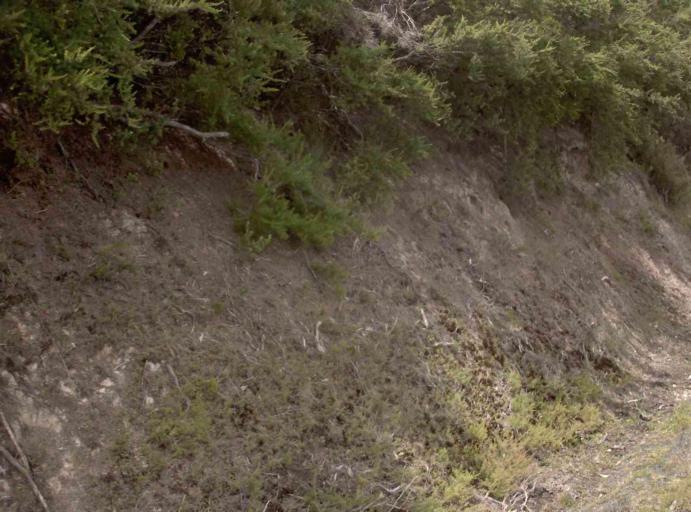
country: AU
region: Victoria
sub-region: Latrobe
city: Morwell
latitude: -39.0123
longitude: 146.2987
